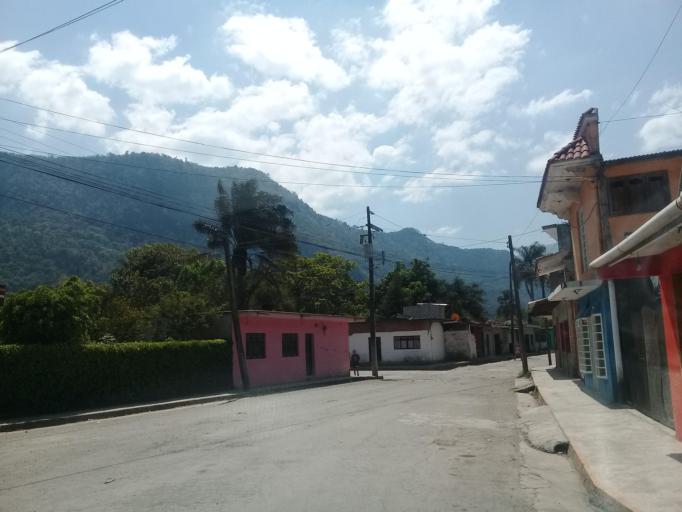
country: MX
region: Veracruz
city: Jalapilla
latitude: 18.8098
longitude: -97.0709
